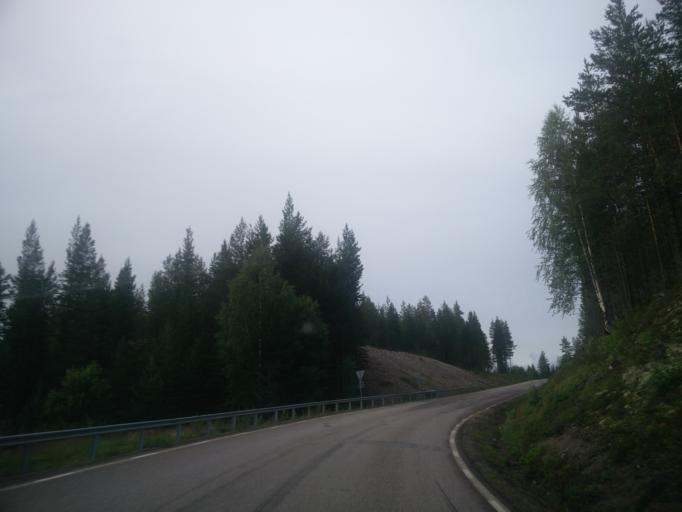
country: NO
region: Hedmark
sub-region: Trysil
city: Innbygda
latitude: 61.7972
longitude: 12.9202
